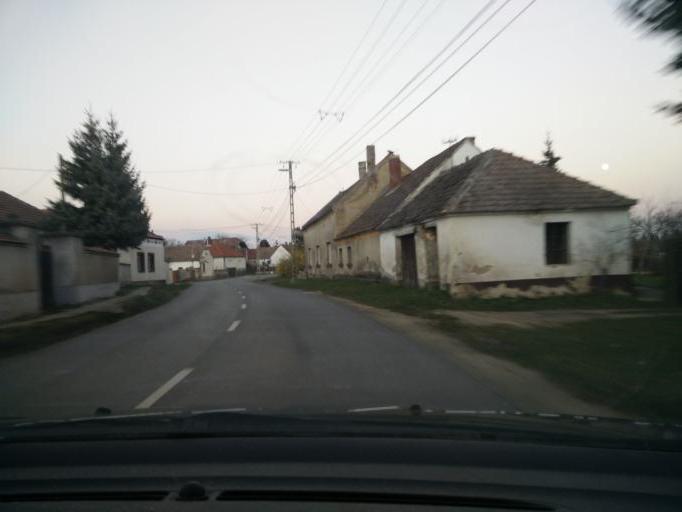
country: HU
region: Veszprem
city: Devecser
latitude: 47.0697
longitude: 17.3620
